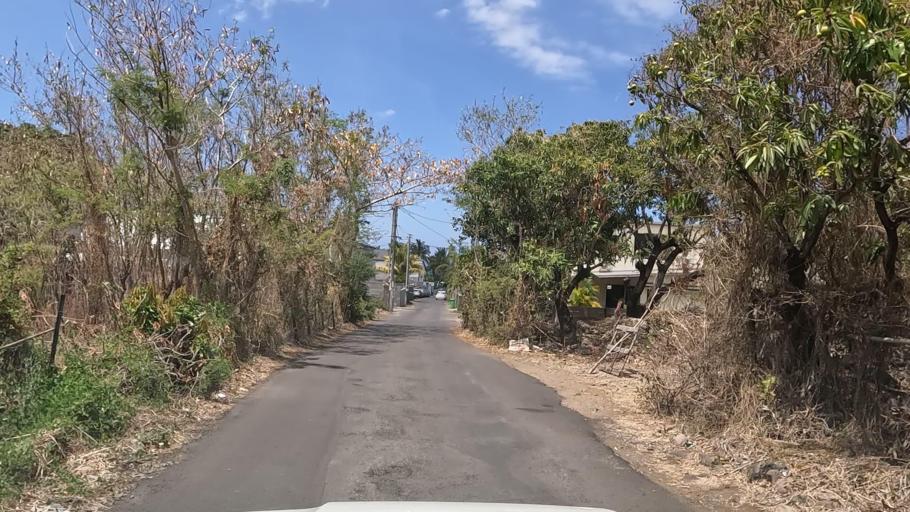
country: RE
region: Reunion
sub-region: Reunion
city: Saint-Louis
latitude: -21.2796
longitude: 55.4443
